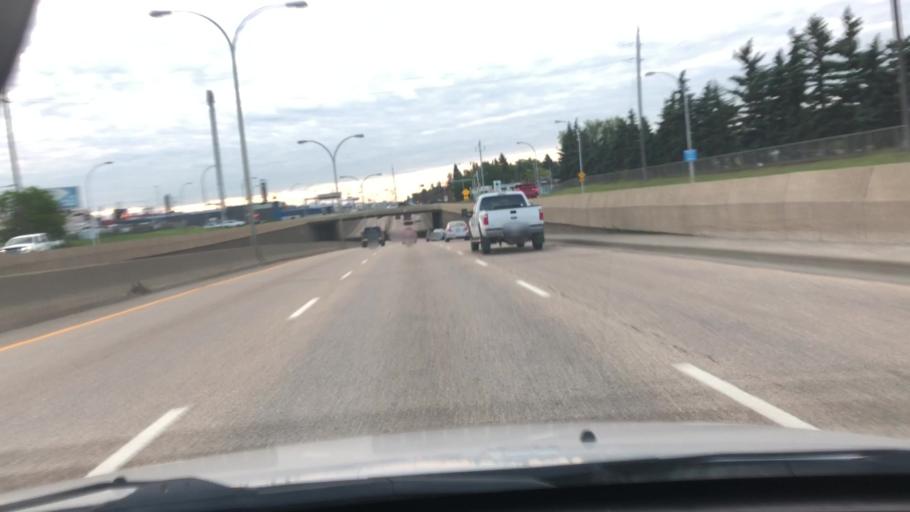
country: CA
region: Alberta
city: Edmonton
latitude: 53.5813
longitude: -113.4954
